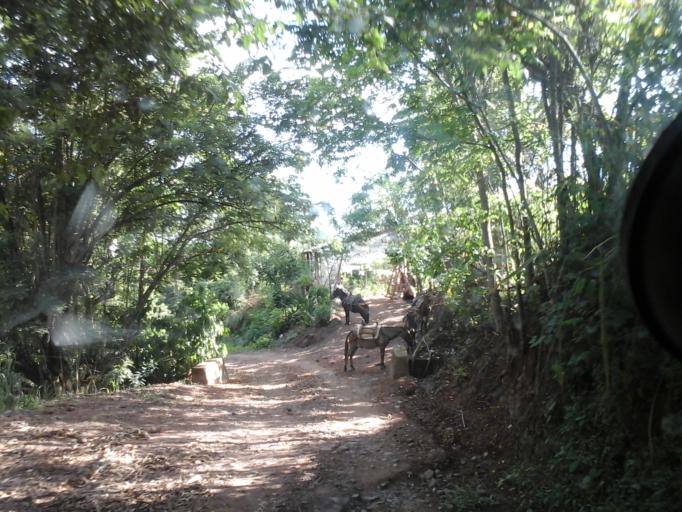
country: CO
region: Cesar
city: San Diego
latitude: 10.2666
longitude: -73.1015
